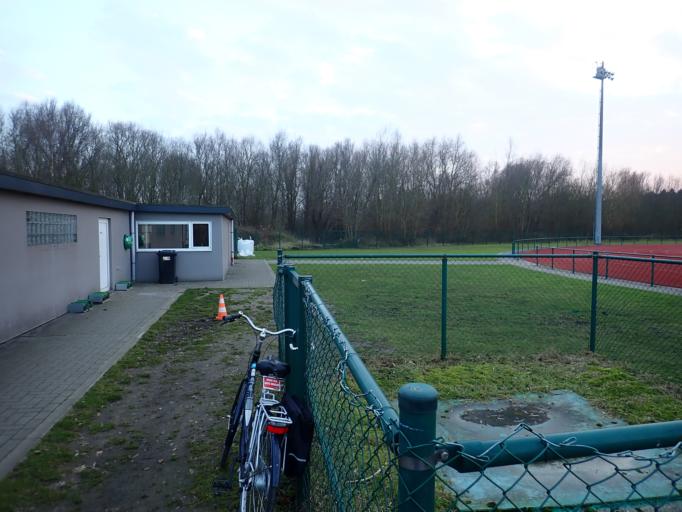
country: BE
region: Flanders
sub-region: Provincie Antwerpen
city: Borsbeek
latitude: 51.2155
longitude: 4.4852
